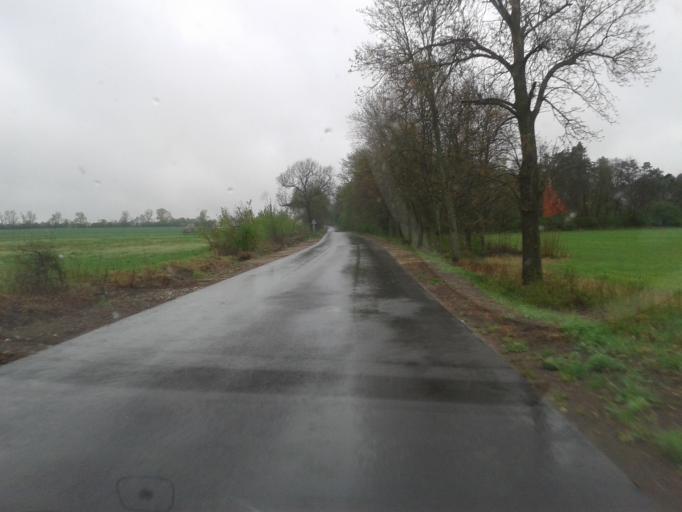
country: PL
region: Lublin Voivodeship
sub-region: Powiat tomaszowski
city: Jarczow
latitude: 50.3646
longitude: 23.5755
